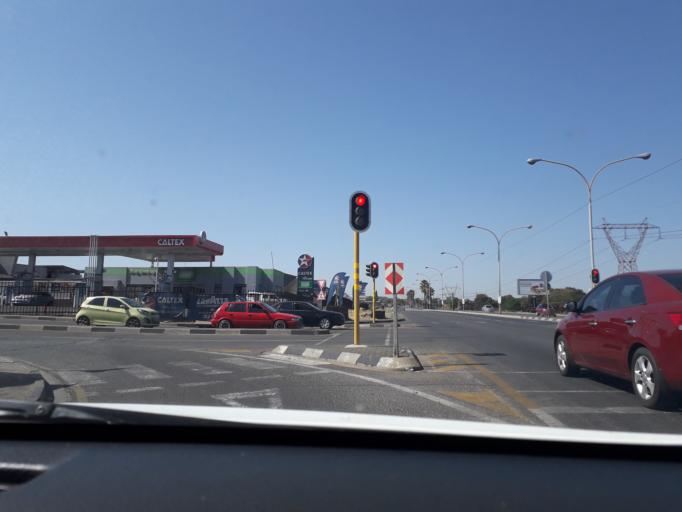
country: ZA
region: Gauteng
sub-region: City of Johannesburg Metropolitan Municipality
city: Modderfontein
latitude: -26.1042
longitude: 28.2215
